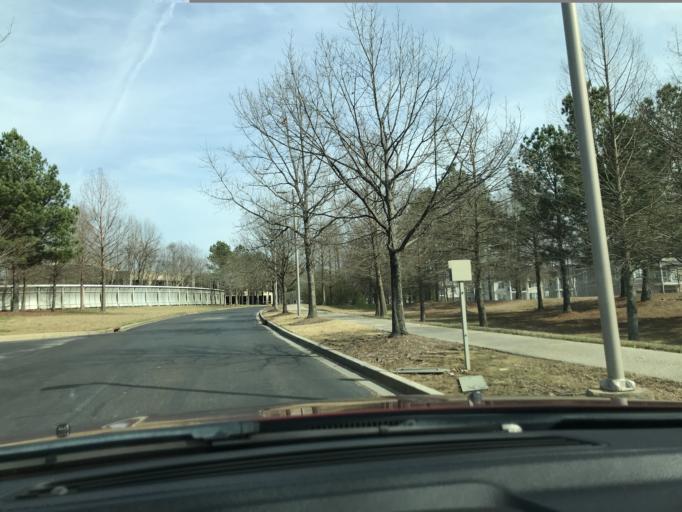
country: US
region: Tennessee
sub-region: Shelby County
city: Collierville
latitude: 35.0322
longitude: -89.7227
